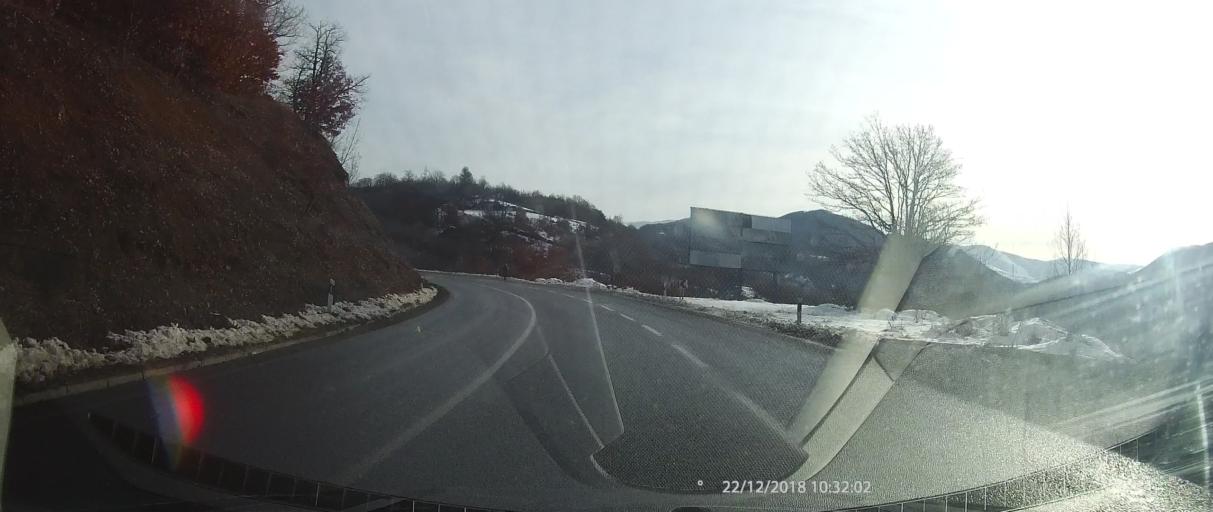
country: MK
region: Kriva Palanka
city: Kriva Palanka
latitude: 42.2206
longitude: 22.4299
